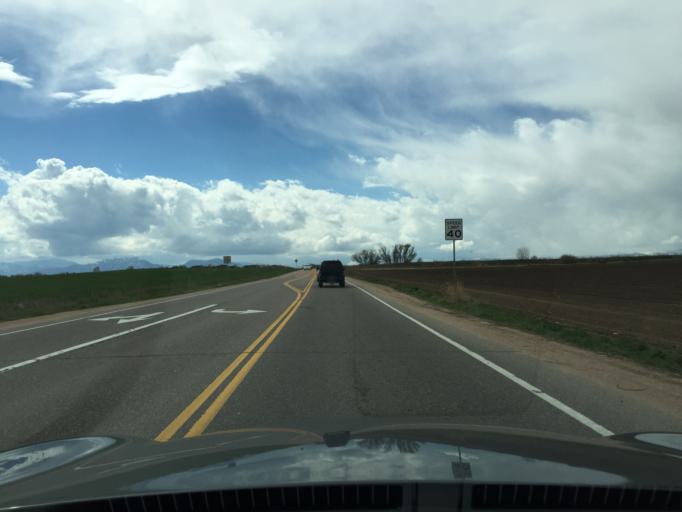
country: US
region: Colorado
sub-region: Boulder County
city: Lafayette
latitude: 40.0149
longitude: -105.0748
